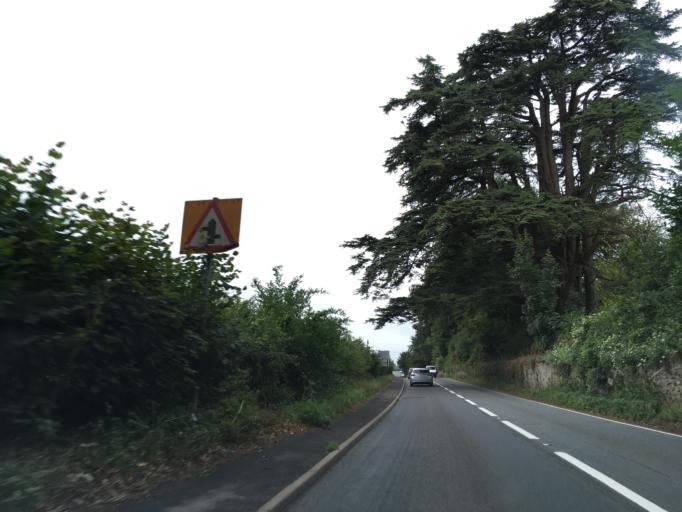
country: GB
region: England
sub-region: Bath and North East Somerset
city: East Harptree
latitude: 51.2708
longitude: -2.5849
